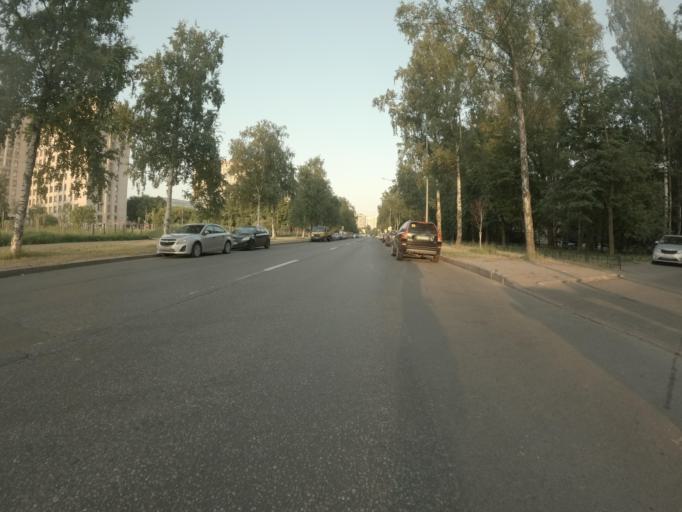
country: RU
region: Leningrad
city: Kalininskiy
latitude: 59.9787
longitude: 30.4266
